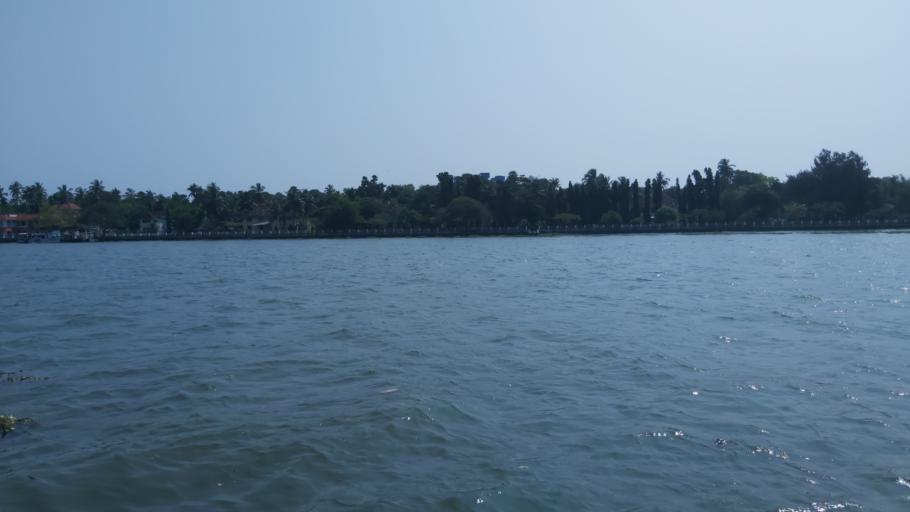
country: IN
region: Kerala
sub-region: Ernakulam
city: Cochin
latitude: 9.9720
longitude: 76.2616
